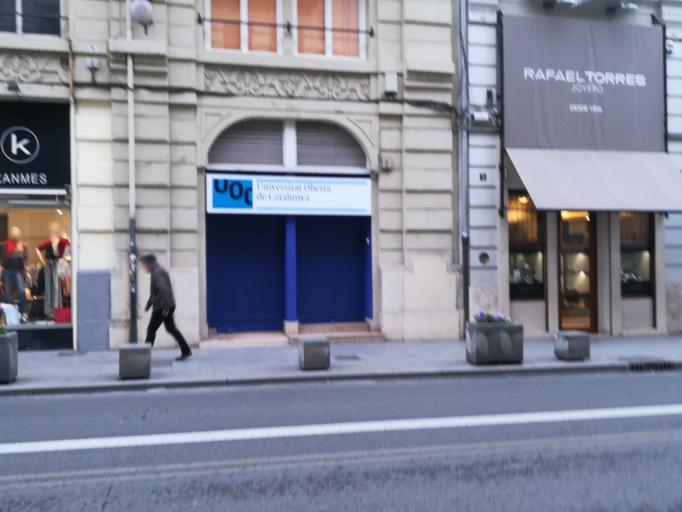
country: ES
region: Valencia
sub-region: Provincia de Valencia
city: Valencia
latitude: 39.4738
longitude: -0.3746
